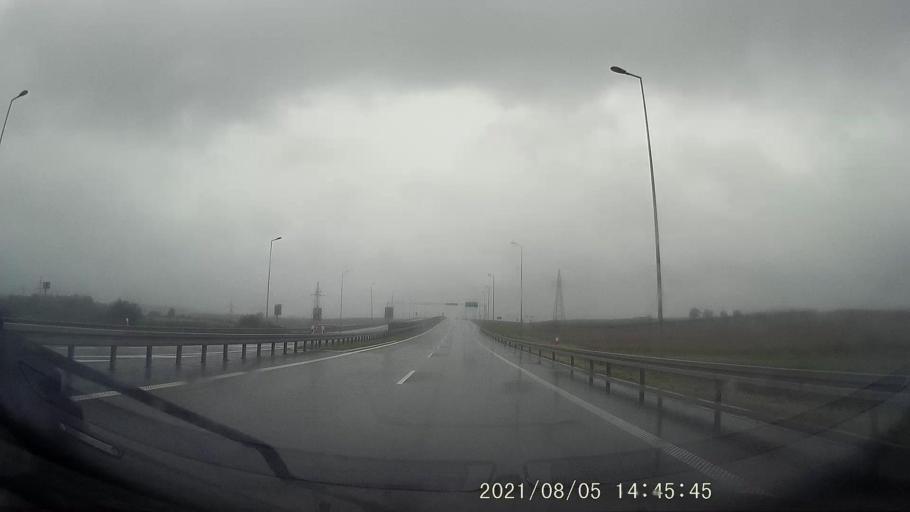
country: PL
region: Opole Voivodeship
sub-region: Powiat nyski
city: Nysa
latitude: 50.5000
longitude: 17.3531
